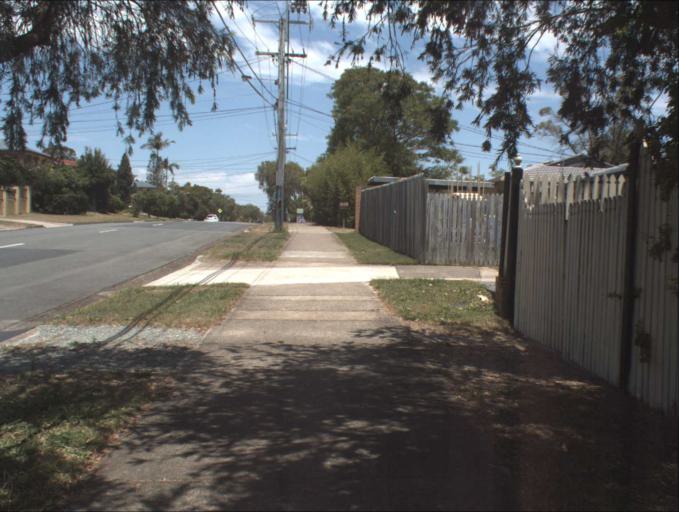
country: AU
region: Queensland
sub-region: Logan
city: Rochedale South
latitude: -27.5903
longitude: 153.1383
